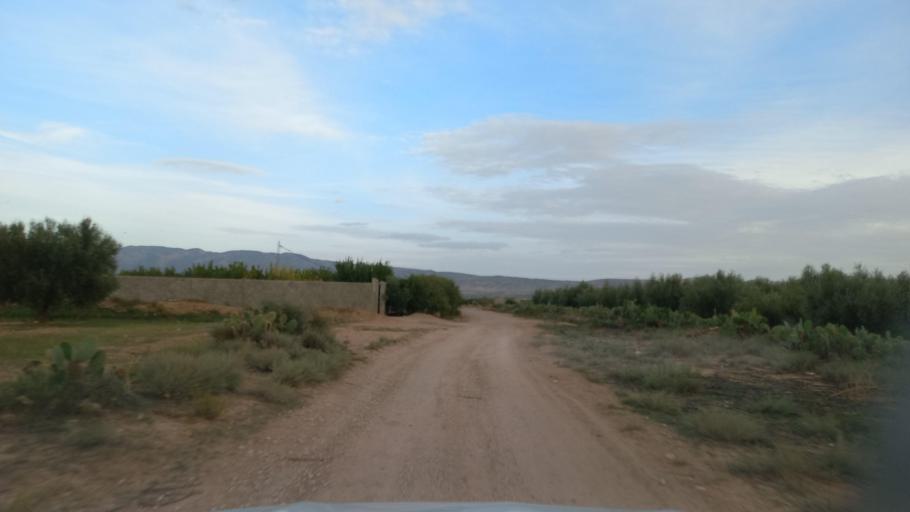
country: TN
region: Al Qasrayn
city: Sbiba
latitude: 35.4224
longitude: 9.1051
